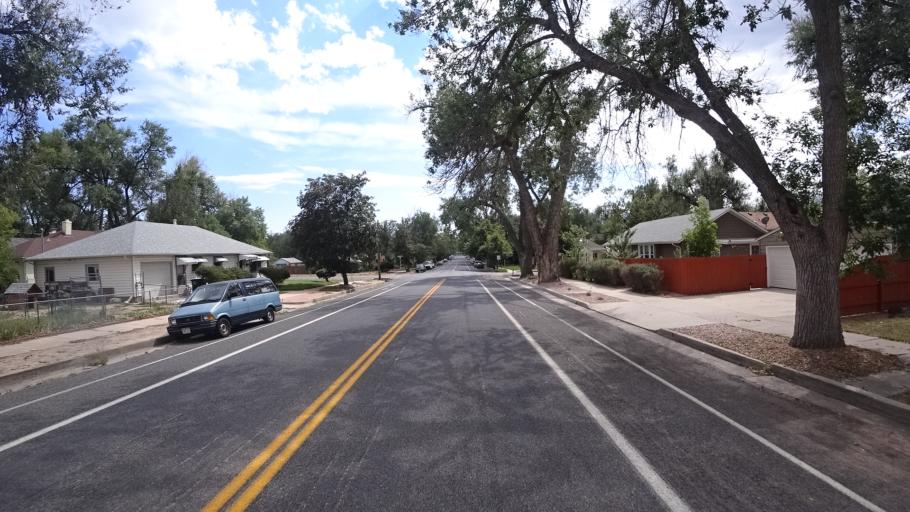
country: US
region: Colorado
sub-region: El Paso County
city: Colorado Springs
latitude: 38.8452
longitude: -104.8077
